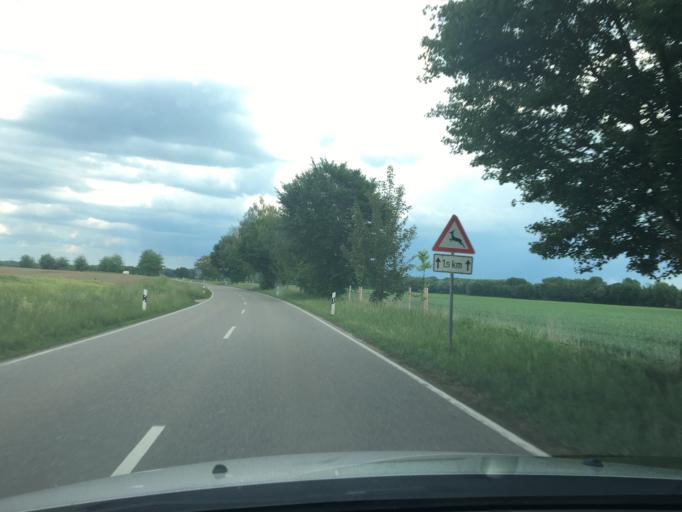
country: DE
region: Bavaria
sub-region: Upper Bavaria
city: Haimhausen
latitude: 48.3147
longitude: 11.5153
